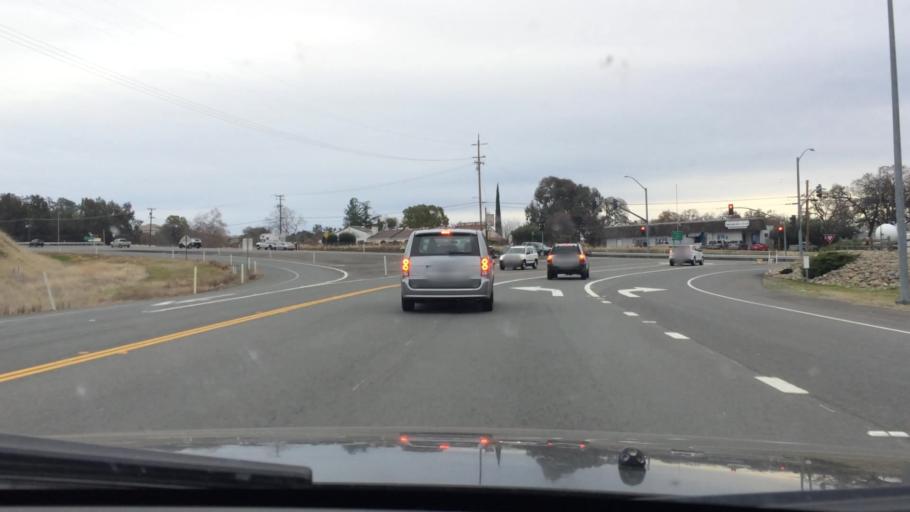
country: US
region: California
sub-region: Amador County
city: Jackson
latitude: 38.3661
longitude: -120.7951
